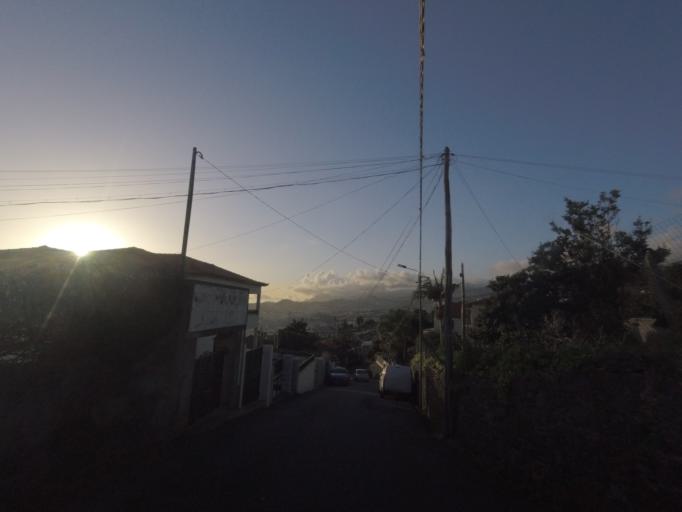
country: PT
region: Madeira
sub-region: Funchal
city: Nossa Senhora do Monte
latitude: 32.6544
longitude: -16.8876
